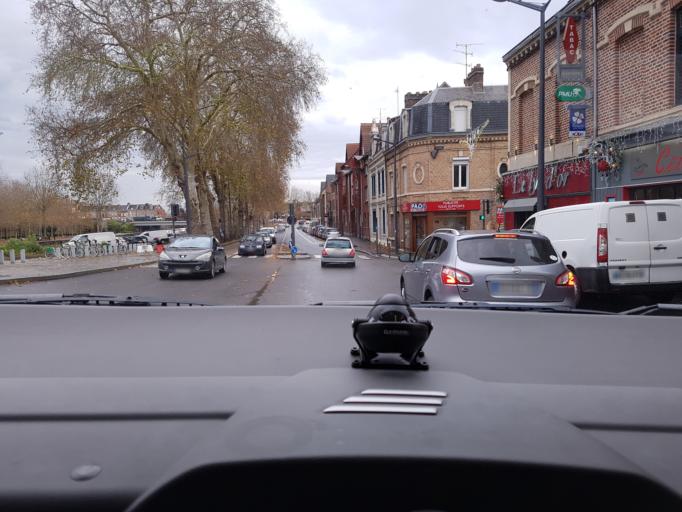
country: FR
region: Picardie
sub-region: Departement de la Somme
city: Amiens
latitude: 49.8953
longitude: 2.3059
